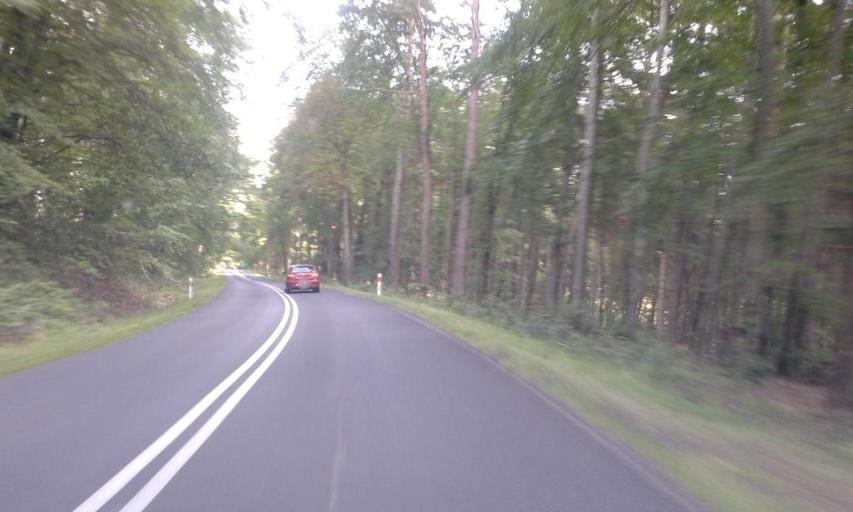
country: PL
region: West Pomeranian Voivodeship
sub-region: Powiat koszalinski
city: Polanow
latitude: 54.2387
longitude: 16.7099
